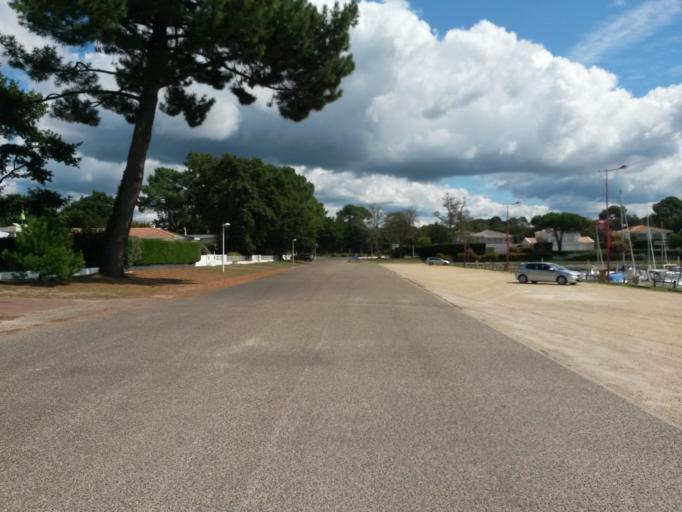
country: FR
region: Aquitaine
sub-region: Departement de la Gironde
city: Andernos-les-Bains
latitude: 44.7232
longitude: -1.0766
